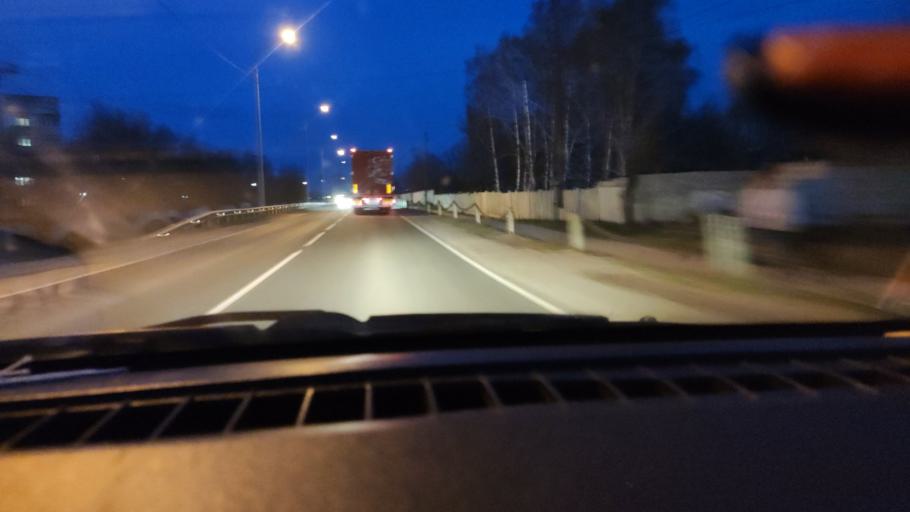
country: RU
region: Saratov
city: Sennoy
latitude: 52.1519
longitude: 46.9620
